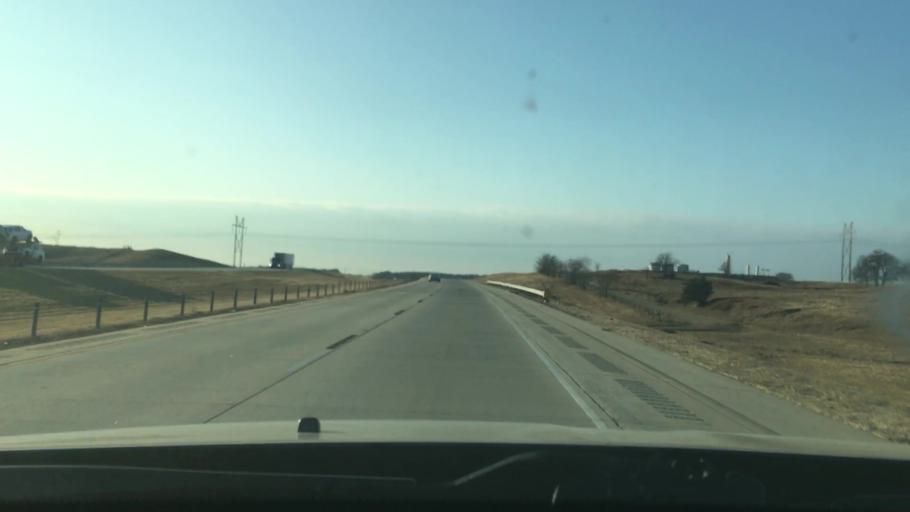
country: US
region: Oklahoma
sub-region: Carter County
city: Ardmore
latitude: 34.2558
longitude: -97.1653
